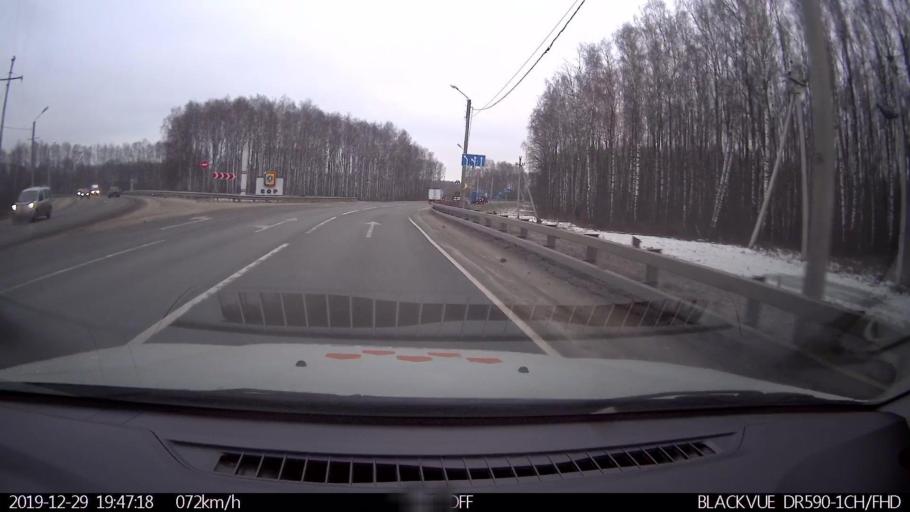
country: RU
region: Nizjnij Novgorod
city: Neklyudovo
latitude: 56.3947
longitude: 44.0066
